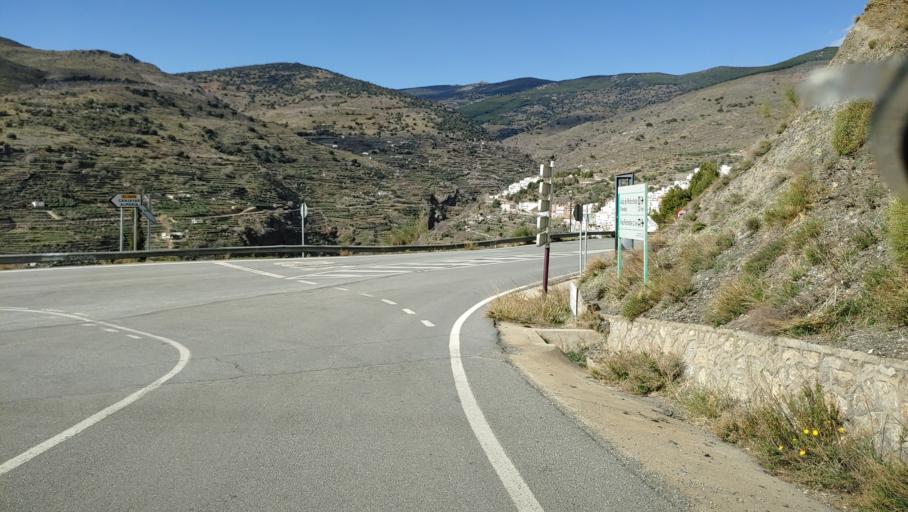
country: ES
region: Andalusia
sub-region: Provincia de Almeria
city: Ohanes
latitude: 37.0341
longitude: -2.7427
